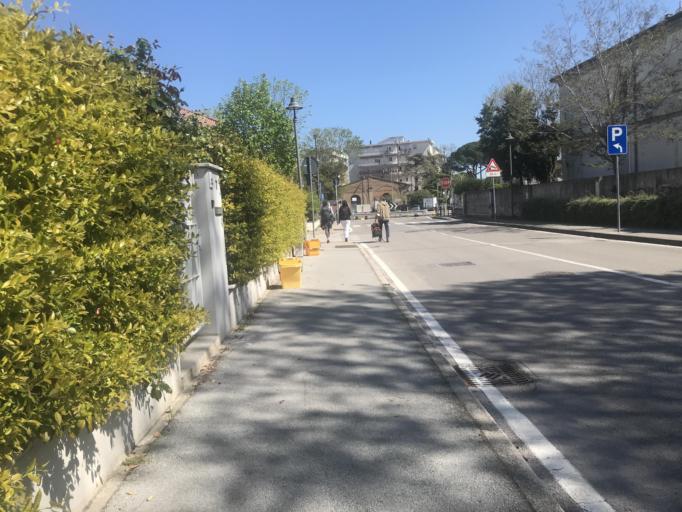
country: IT
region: Emilia-Romagna
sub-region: Provincia di Rimini
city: Rimini
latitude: 44.0720
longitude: 12.5715
